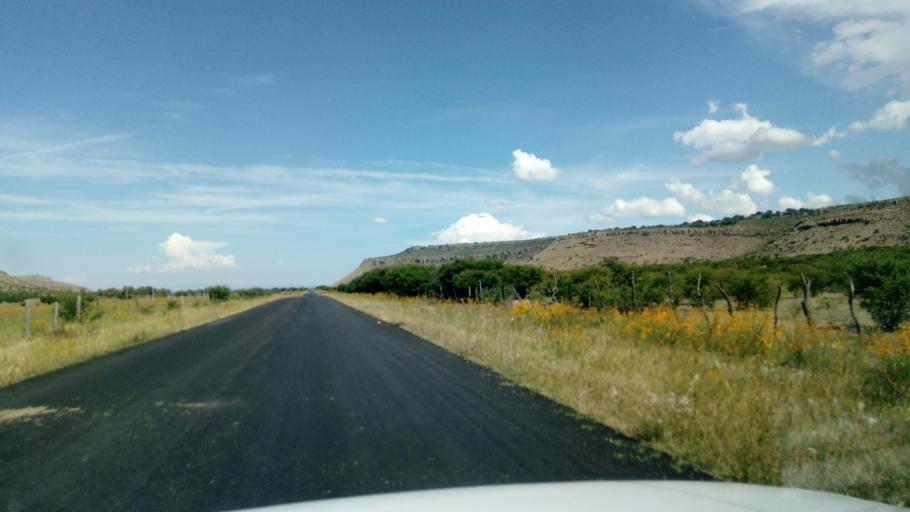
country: MX
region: Durango
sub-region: Durango
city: Jose Refugio Salcido
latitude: 23.8056
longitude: -104.4841
